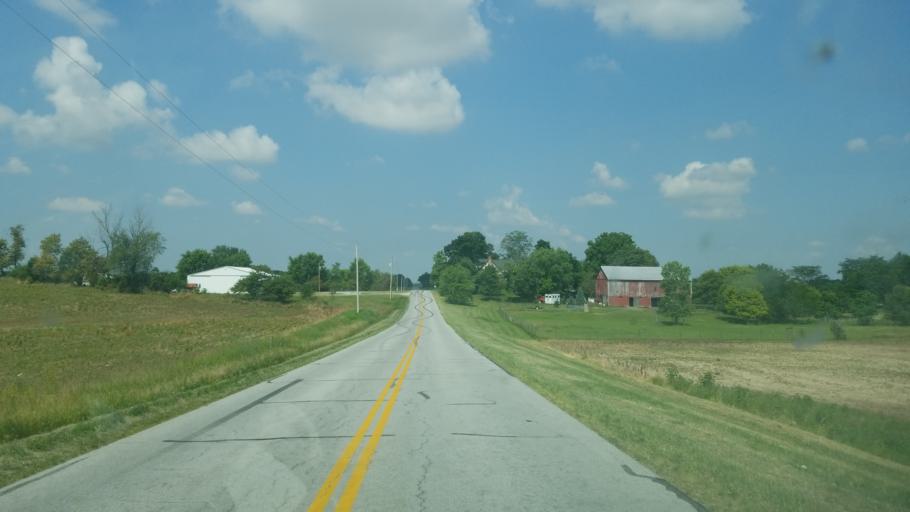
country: US
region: Ohio
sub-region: Auglaize County
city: Cridersville
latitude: 40.5714
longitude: -84.0495
